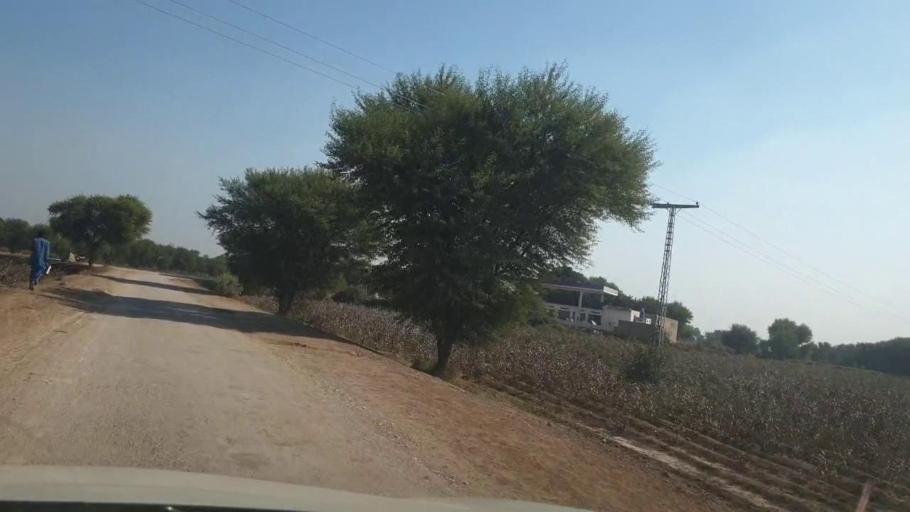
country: PK
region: Sindh
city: Bhan
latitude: 26.5794
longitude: 67.7066
